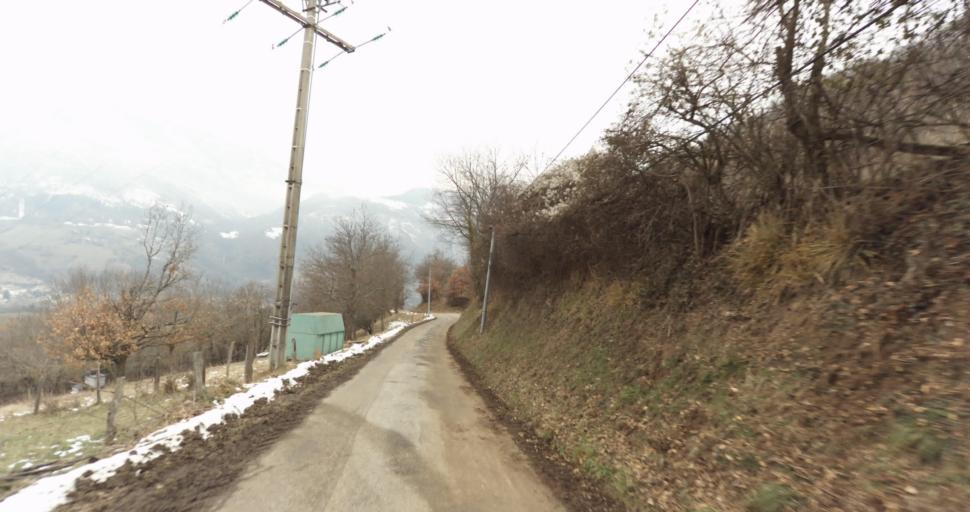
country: FR
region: Rhone-Alpes
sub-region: Departement de l'Isere
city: Vif
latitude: 45.0190
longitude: 5.6654
